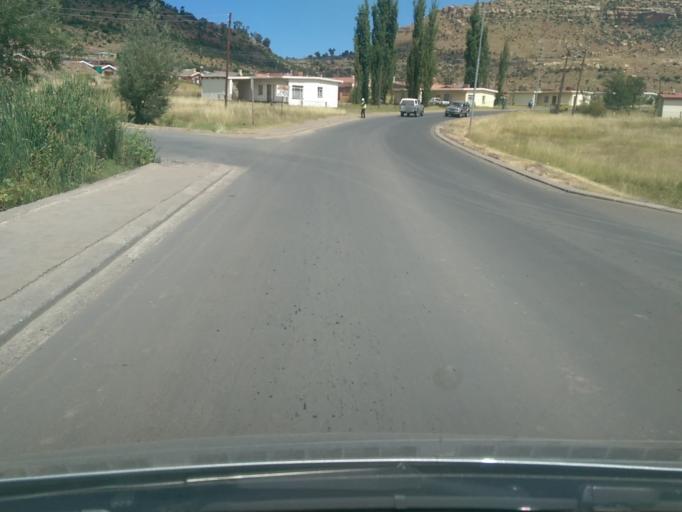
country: LS
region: Maseru
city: Maseru
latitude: -29.3277
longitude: 27.4867
